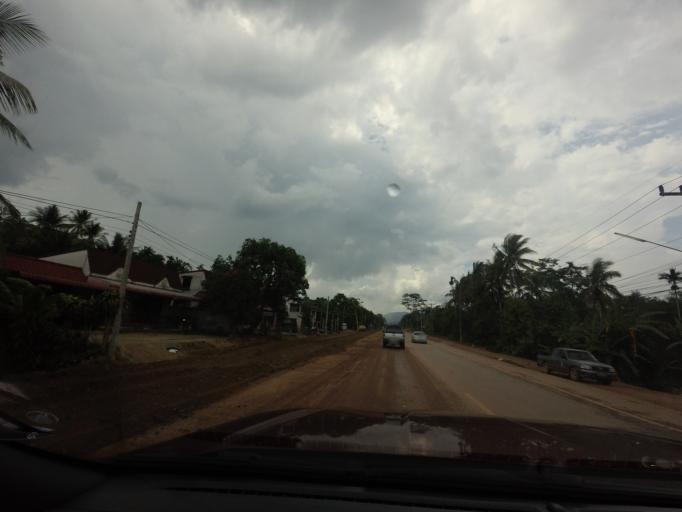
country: TH
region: Yala
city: Ban Nang Sata
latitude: 6.3197
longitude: 101.3036
